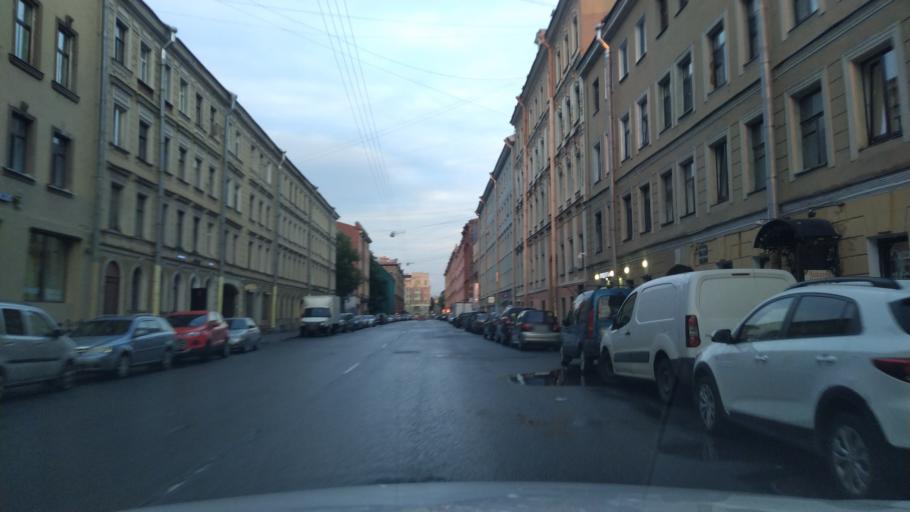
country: RU
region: St.-Petersburg
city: Saint Petersburg
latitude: 59.9286
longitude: 30.3257
